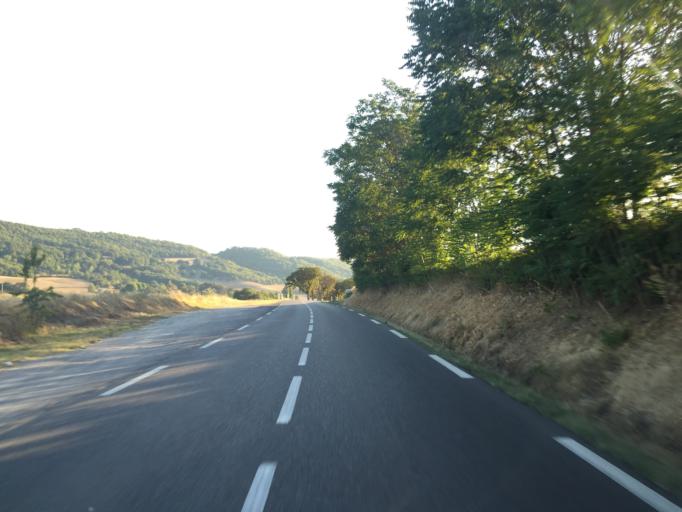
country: FR
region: Provence-Alpes-Cote d'Azur
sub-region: Departement des Alpes-de-Haute-Provence
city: Reillanne
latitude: 43.8607
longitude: 5.6540
